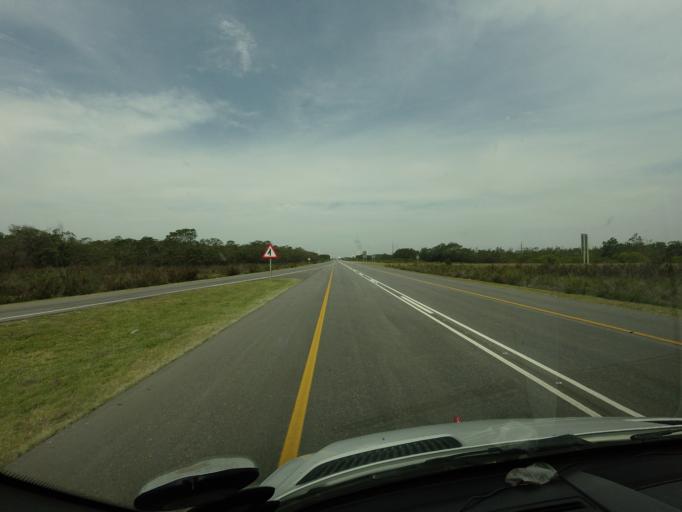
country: ZA
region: Eastern Cape
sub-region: Cacadu District Municipality
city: Kruisfontein
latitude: -34.0075
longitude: 24.7821
